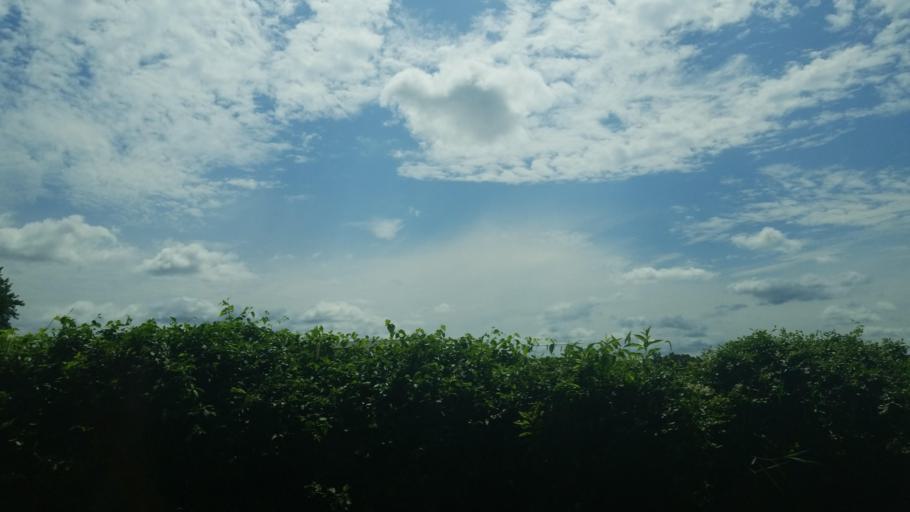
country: US
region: Illinois
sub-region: Williamson County
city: Johnston City
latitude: 37.7870
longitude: -88.7816
